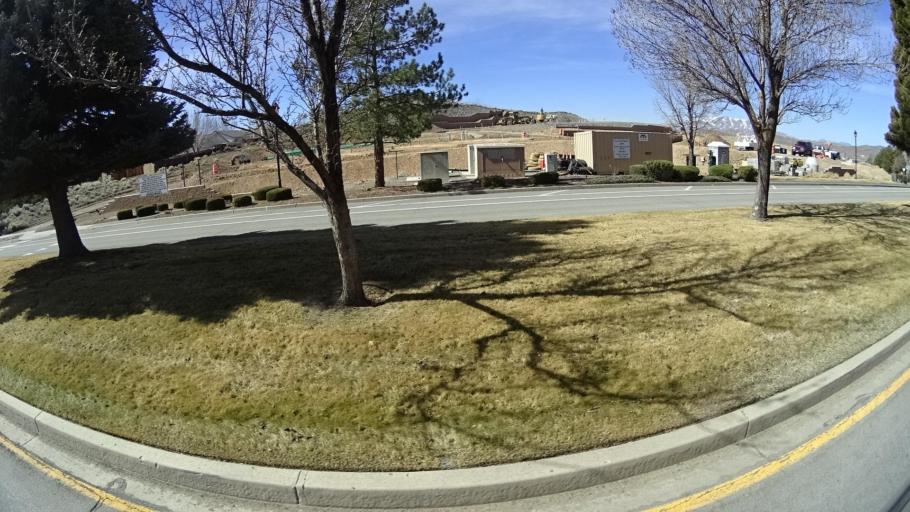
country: US
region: Nevada
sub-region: Washoe County
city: Sparks
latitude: 39.5786
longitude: -119.6994
